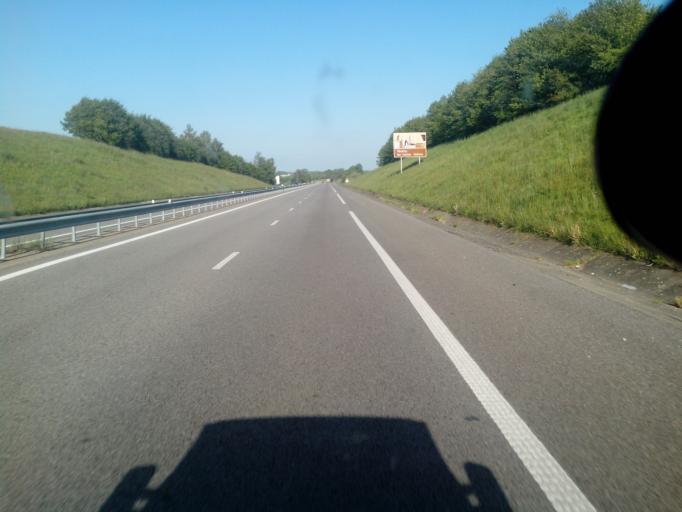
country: FR
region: Haute-Normandie
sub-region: Departement de la Seine-Maritime
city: Saint-Romain-de-Colbosc
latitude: 49.5699
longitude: 0.3784
